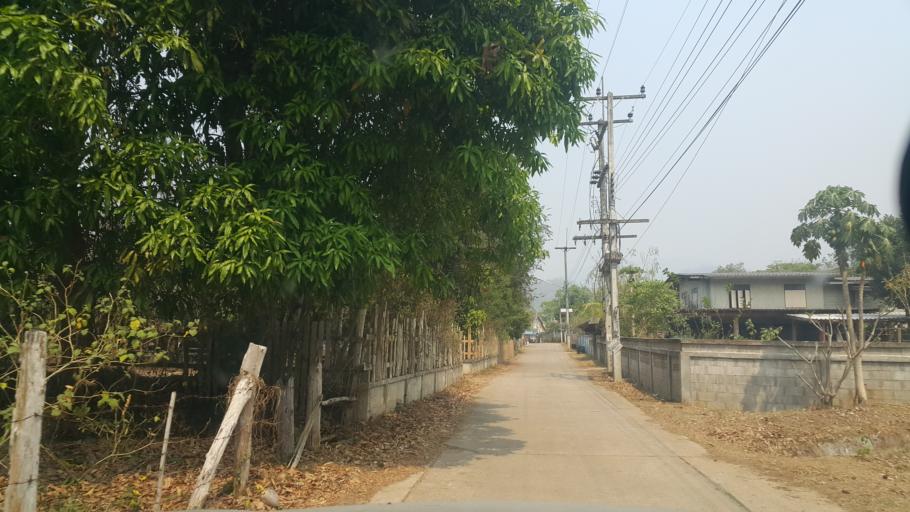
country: TH
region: Lampang
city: Sop Prap
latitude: 17.8034
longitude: 99.2593
